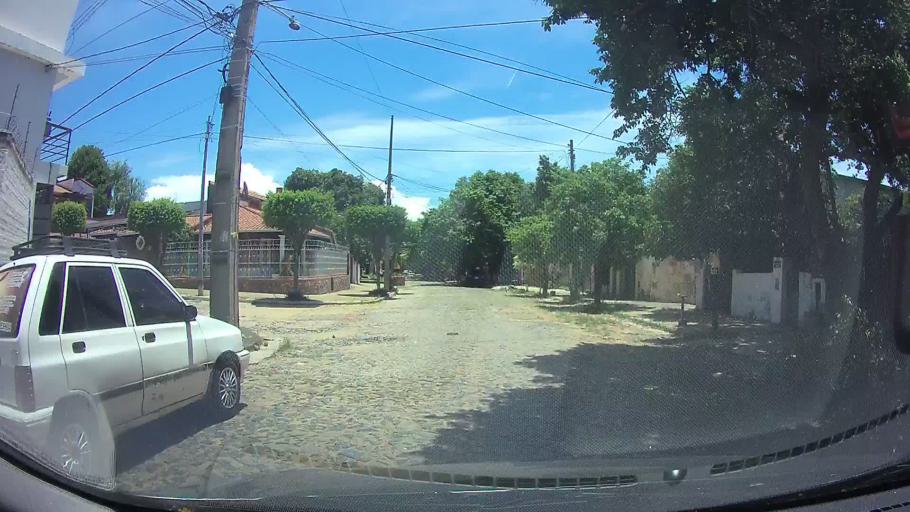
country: PY
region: Asuncion
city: Asuncion
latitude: -25.2712
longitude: -57.6004
